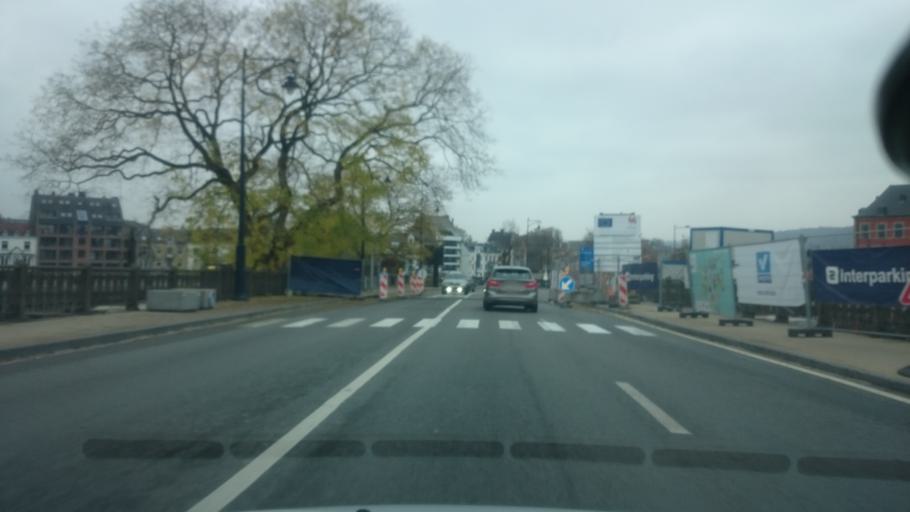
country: BE
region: Wallonia
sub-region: Province de Namur
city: Namur
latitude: 50.4621
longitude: 4.8696
